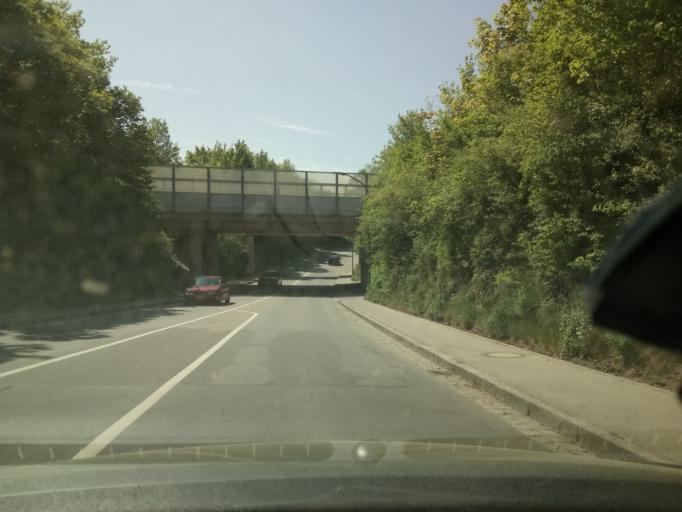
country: DE
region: Bavaria
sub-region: Upper Bavaria
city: Ampfing
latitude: 48.2541
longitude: 12.4178
